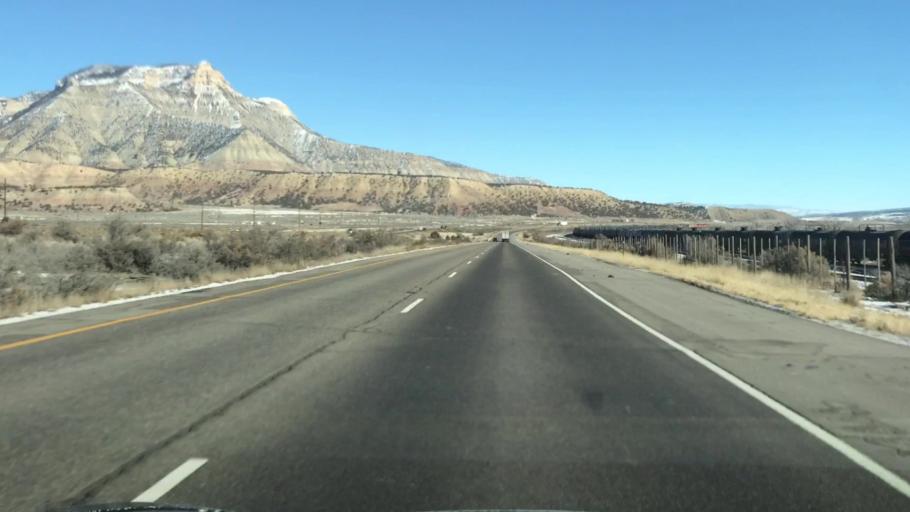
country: US
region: Colorado
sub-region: Garfield County
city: Battlement Mesa
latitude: 39.4710
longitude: -108.0251
